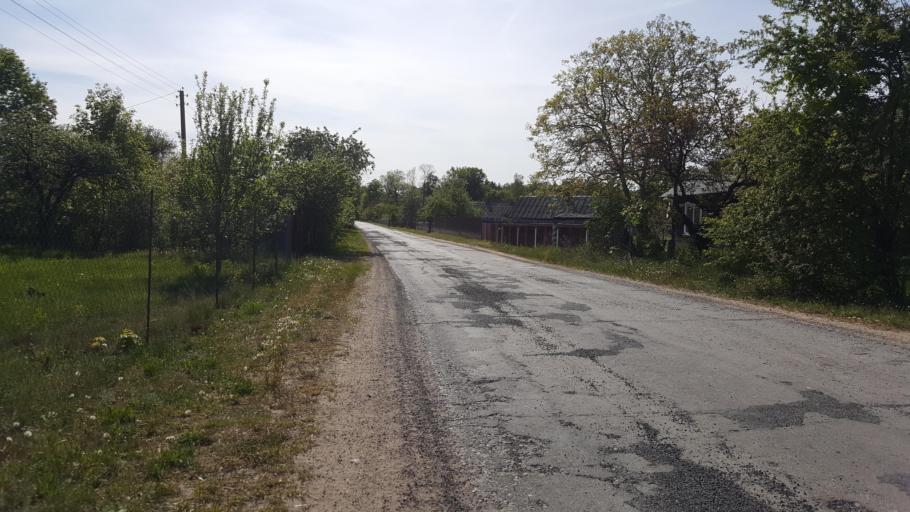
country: BY
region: Brest
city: Zhabinka
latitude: 52.3171
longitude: 24.0087
